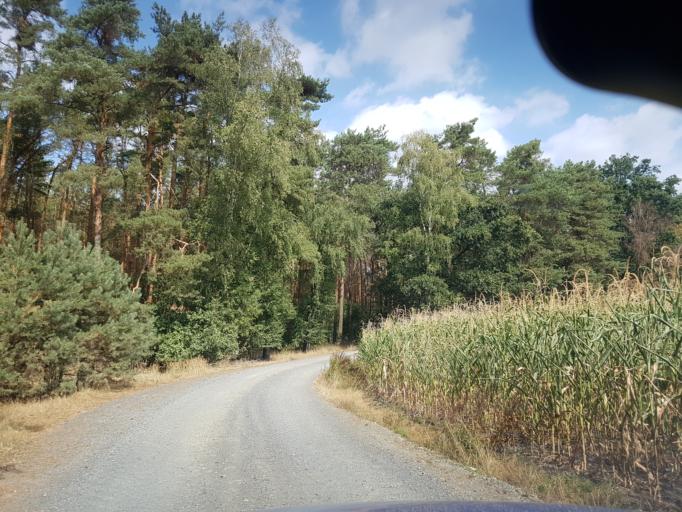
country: DE
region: Brandenburg
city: Bad Liebenwerda
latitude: 51.5496
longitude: 13.3763
